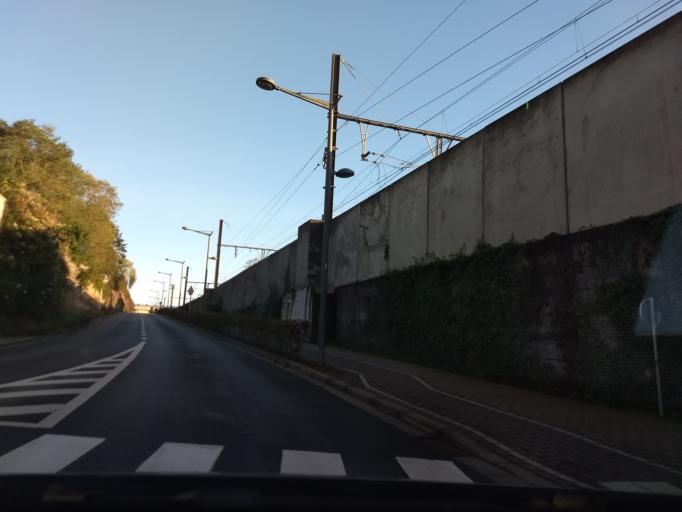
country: BE
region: Wallonia
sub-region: Province du Brabant Wallon
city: Braine-l'Alleud
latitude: 50.6772
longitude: 4.3744
